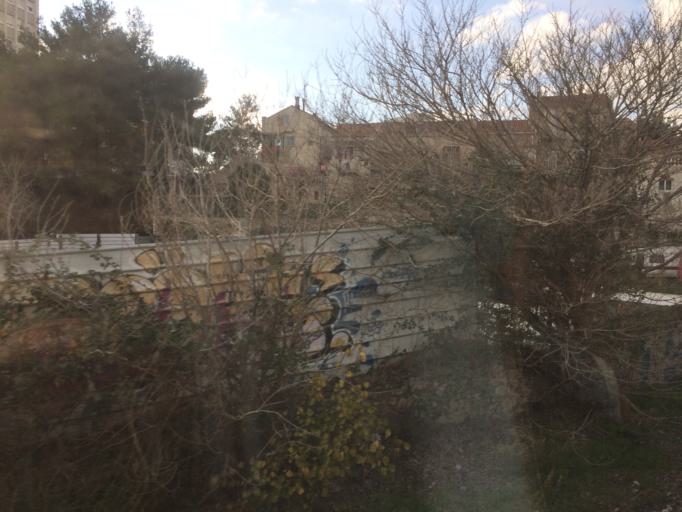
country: FR
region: Provence-Alpes-Cote d'Azur
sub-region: Departement des Bouches-du-Rhone
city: Marseille 14
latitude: 43.3373
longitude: 5.3534
